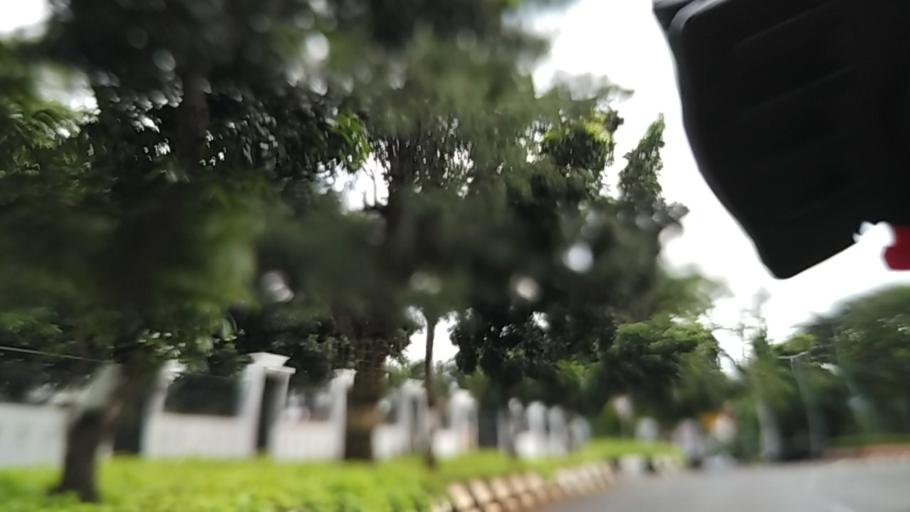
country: ID
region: Central Java
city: Semarang
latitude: -7.0067
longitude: 110.4174
